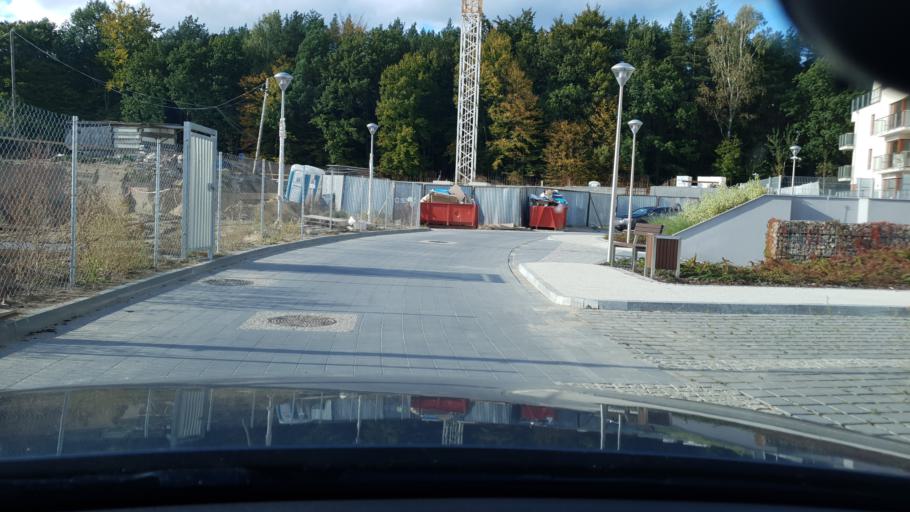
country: PL
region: Pomeranian Voivodeship
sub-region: Powiat kartuski
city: Chwaszczyno
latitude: 54.5013
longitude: 18.4370
